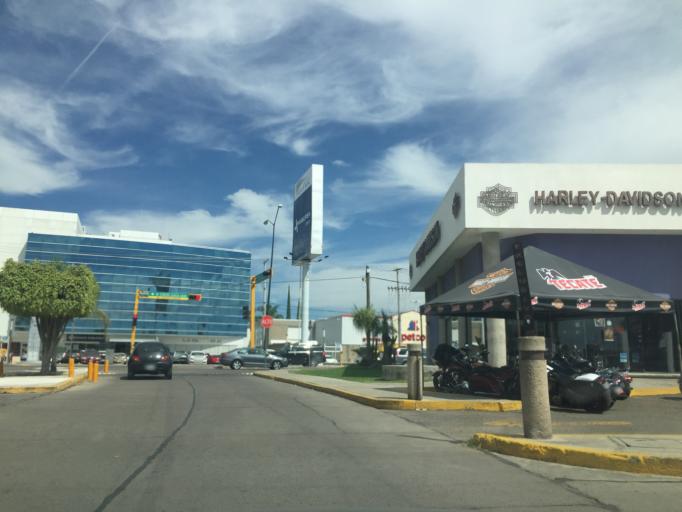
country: MX
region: Guanajuato
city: Leon
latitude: 21.1608
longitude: -101.6937
